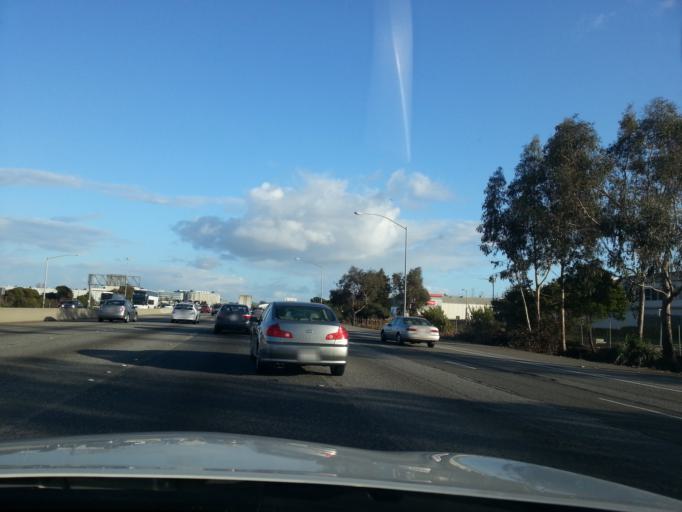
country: US
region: California
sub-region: San Mateo County
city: Millbrae
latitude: 37.6009
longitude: -122.3780
